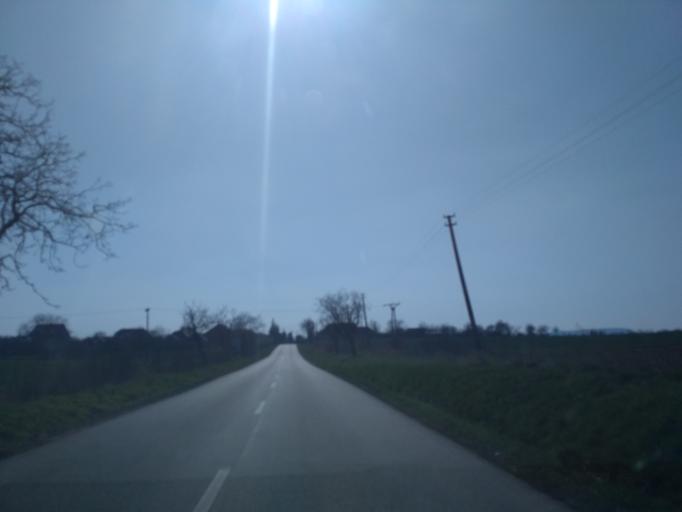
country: SK
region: Kosicky
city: Secovce
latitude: 48.6506
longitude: 21.5803
